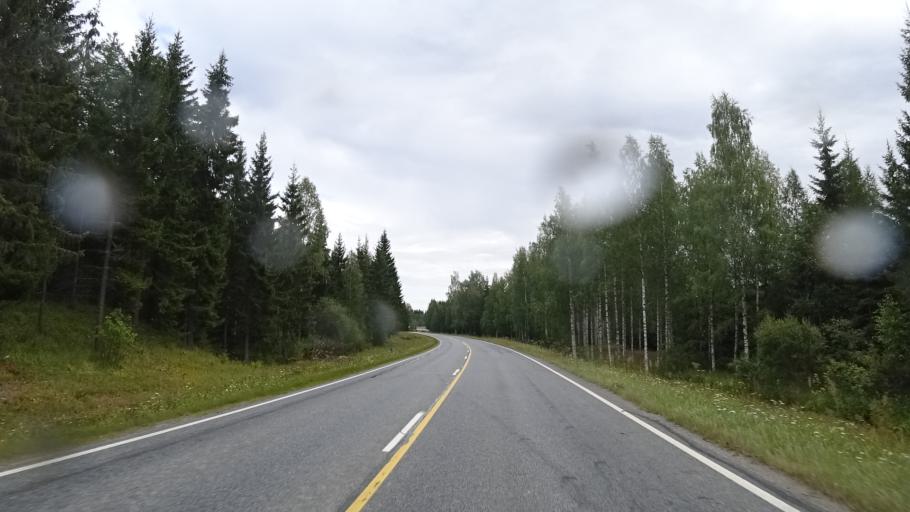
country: FI
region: North Karelia
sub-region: Keski-Karjala
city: Kesaelahti
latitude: 62.1100
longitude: 29.7497
